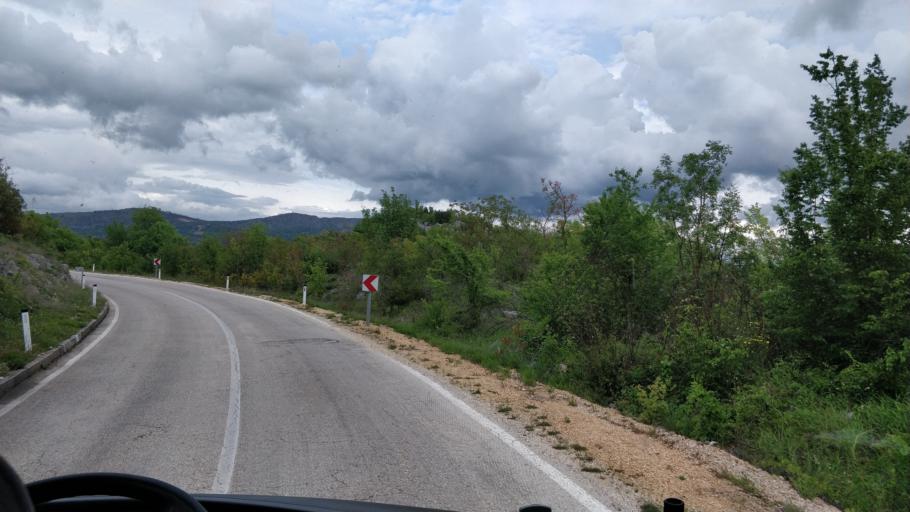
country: BA
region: Federation of Bosnia and Herzegovina
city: Ljubuski
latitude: 43.1735
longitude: 17.4993
